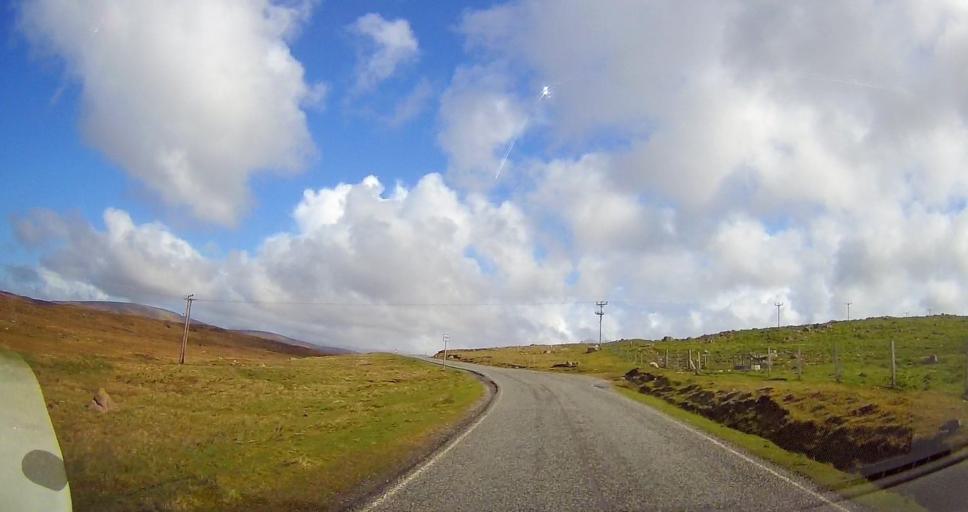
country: GB
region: Scotland
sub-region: Shetland Islands
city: Lerwick
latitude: 60.4807
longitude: -1.4055
